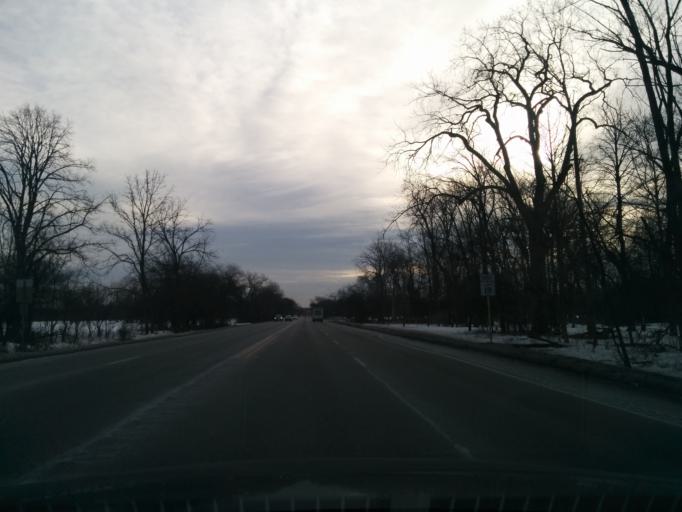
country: US
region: Illinois
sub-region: Cook County
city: Norridge
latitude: 41.9526
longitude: -87.8464
